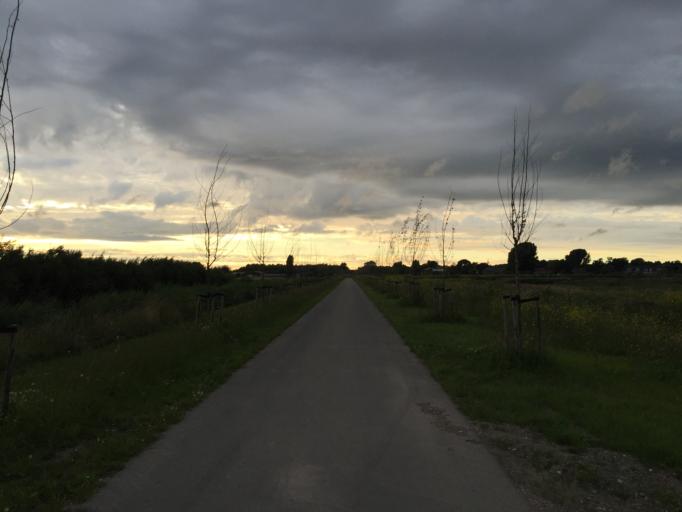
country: NL
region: South Holland
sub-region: Gemeente Pijnacker-Nootdorp
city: Pijnacker
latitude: 52.0290
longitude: 4.4508
